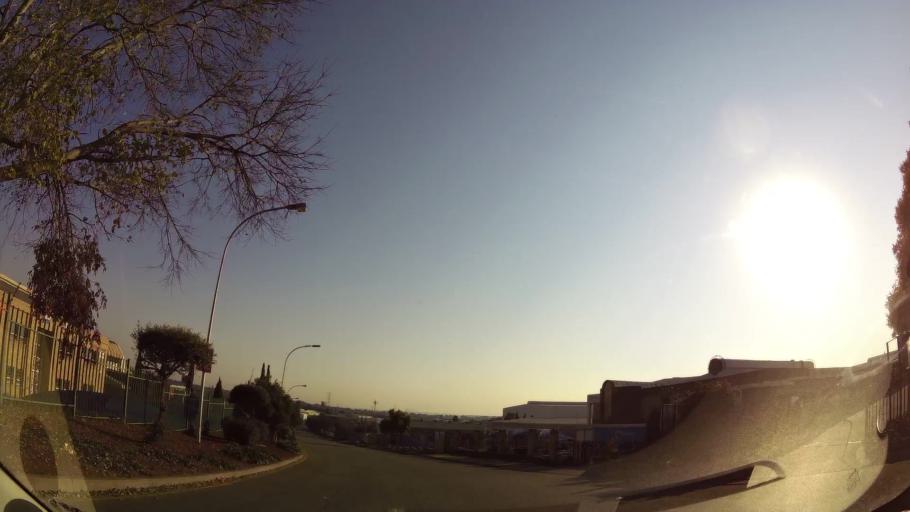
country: ZA
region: Gauteng
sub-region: City of Johannesburg Metropolitan Municipality
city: Modderfontein
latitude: -26.1515
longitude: 28.1843
